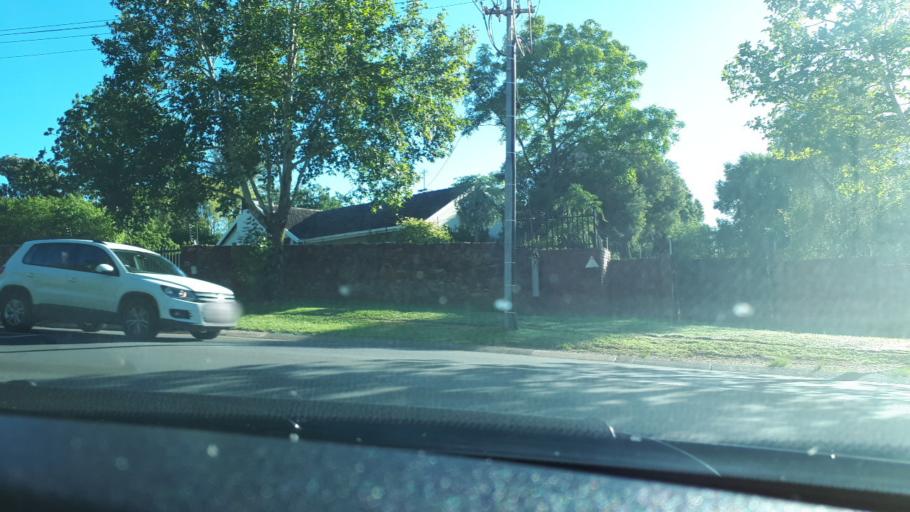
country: ZA
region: Gauteng
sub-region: City of Tshwane Metropolitan Municipality
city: Pretoria
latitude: -25.7744
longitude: 28.2821
